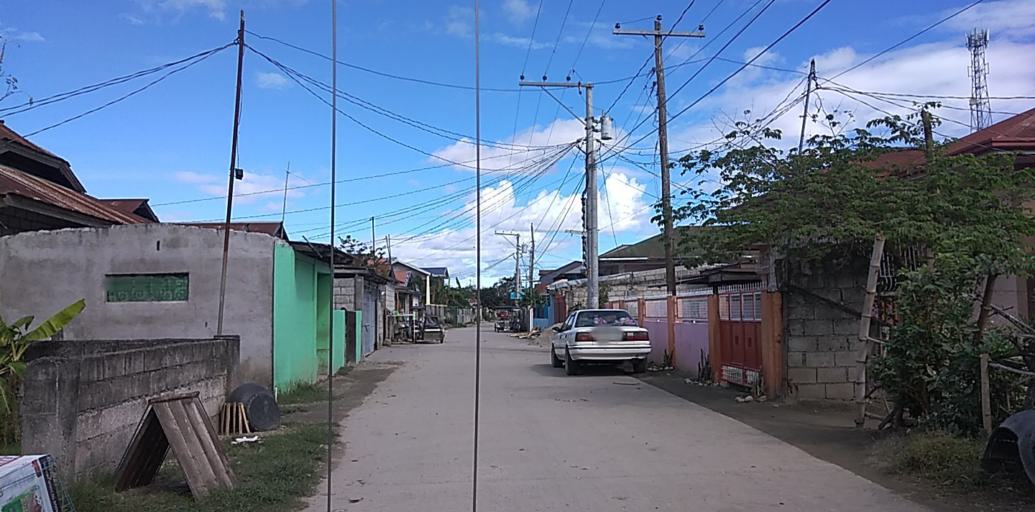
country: PH
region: Central Luzon
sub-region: Province of Pampanga
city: Candating
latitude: 15.1366
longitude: 120.7994
